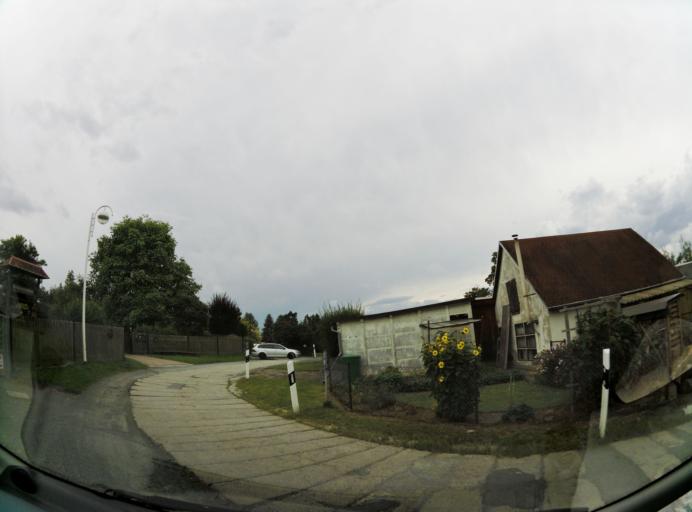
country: DE
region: Thuringia
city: Schleiz
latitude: 50.5770
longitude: 11.8233
